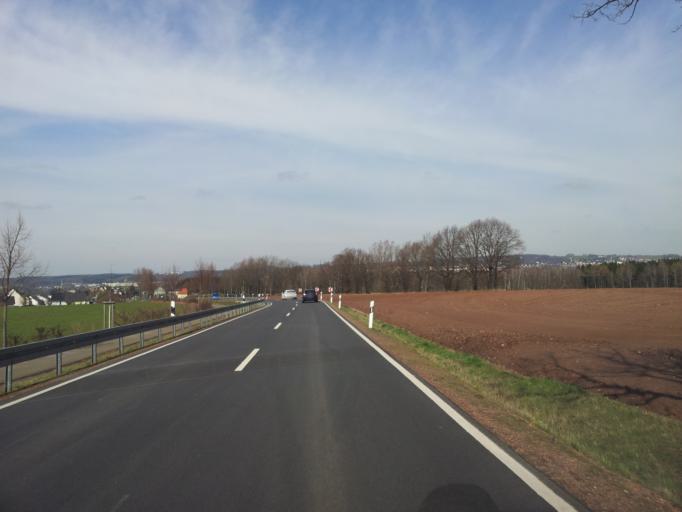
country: DE
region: Saxony
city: Gersdorf
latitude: 50.7633
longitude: 12.7165
